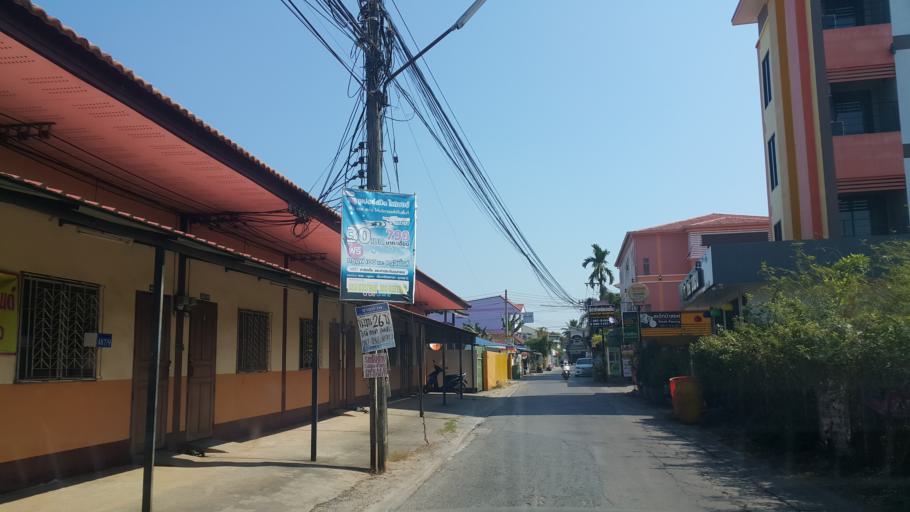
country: TH
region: Changwat Udon Thani
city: Udon Thani
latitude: 17.3921
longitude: 102.8079
